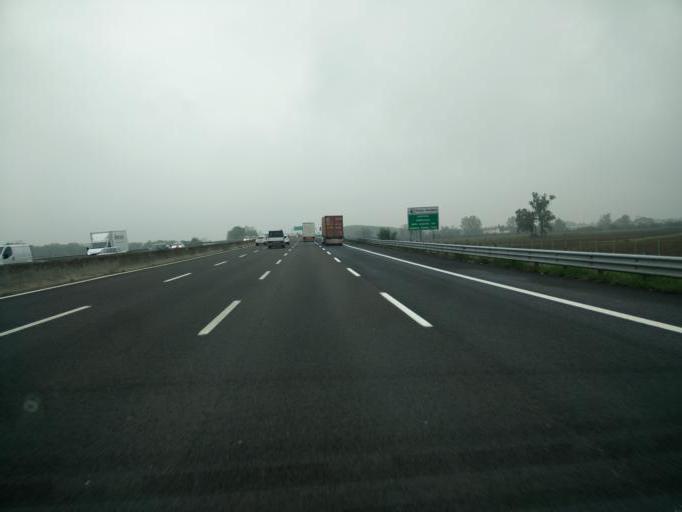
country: IT
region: Emilia-Romagna
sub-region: Provincia di Modena
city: Baggiovara
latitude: 44.6399
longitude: 10.8717
